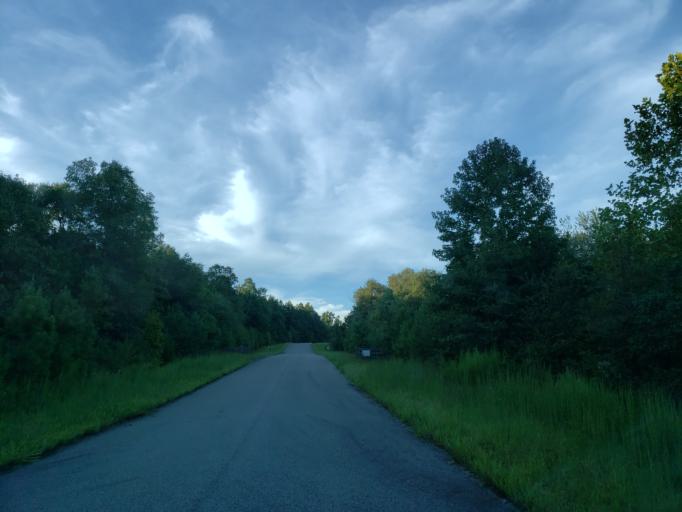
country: US
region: Georgia
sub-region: Bartow County
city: Euharlee
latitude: 34.2387
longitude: -85.0038
